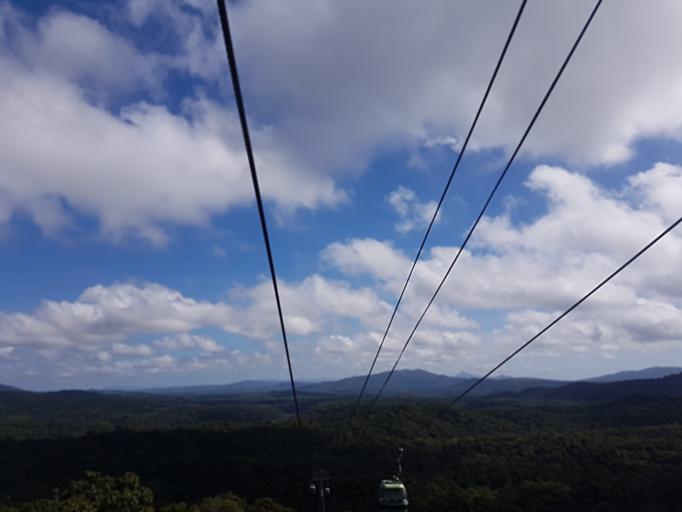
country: AU
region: Queensland
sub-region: Tablelands
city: Kuranda
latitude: -16.8466
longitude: 145.6654
